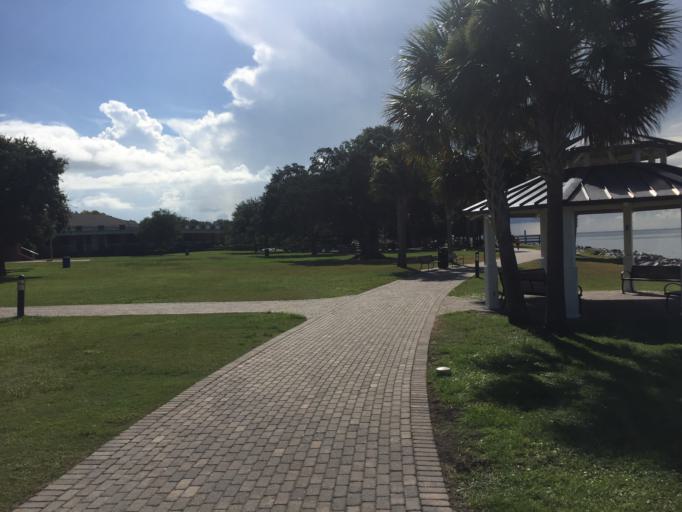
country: US
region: Georgia
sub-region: Glynn County
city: Saint Simons Island
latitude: 31.1341
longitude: -81.3962
